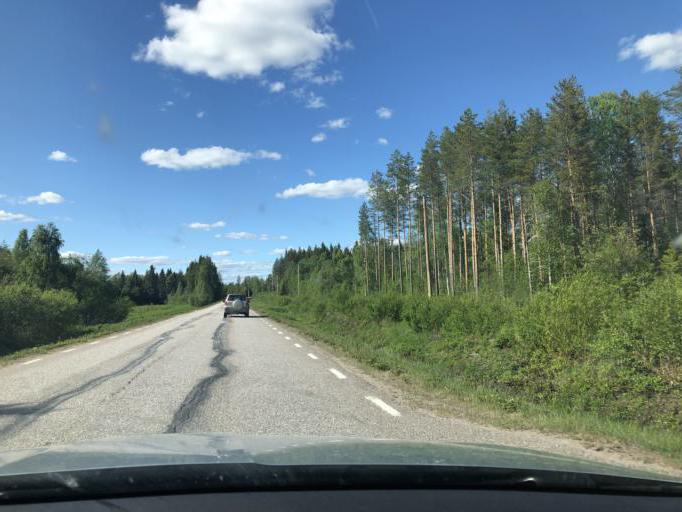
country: SE
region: Norrbotten
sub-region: Kalix Kommun
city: Kalix
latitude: 65.9394
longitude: 23.1567
